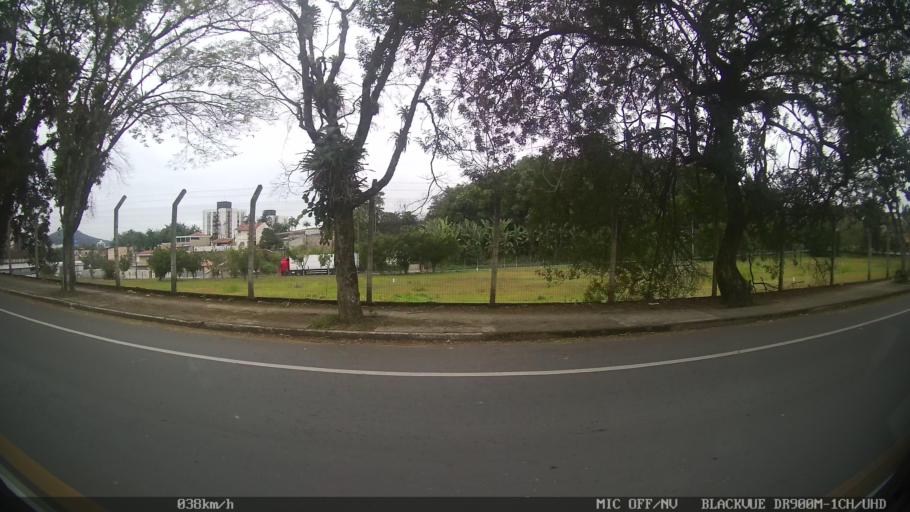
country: BR
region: Santa Catarina
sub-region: Joinville
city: Joinville
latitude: -26.3248
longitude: -48.8497
